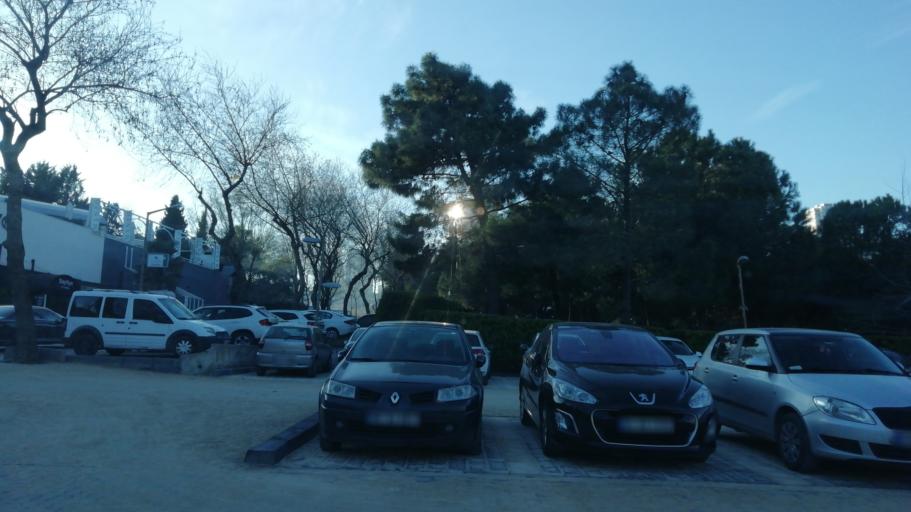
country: TR
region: Istanbul
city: Esenyurt
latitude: 41.0682
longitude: 28.6899
